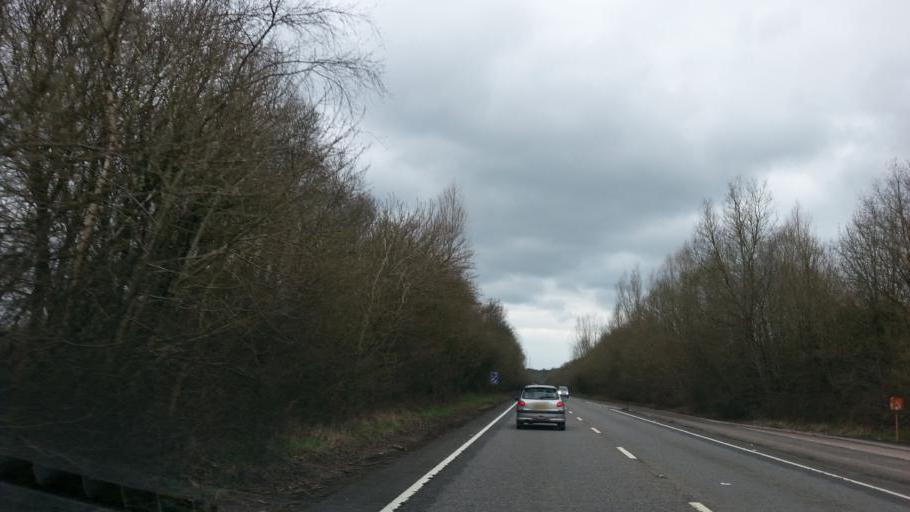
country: GB
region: England
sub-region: Devon
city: Barnstaple
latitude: 51.0596
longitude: -3.9780
